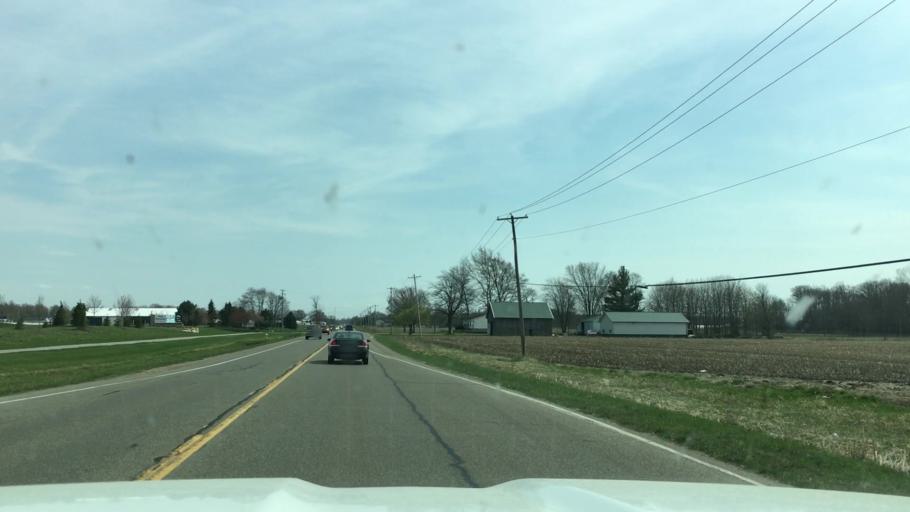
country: US
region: Michigan
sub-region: Ottawa County
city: Hudsonville
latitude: 42.8774
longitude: -85.9013
